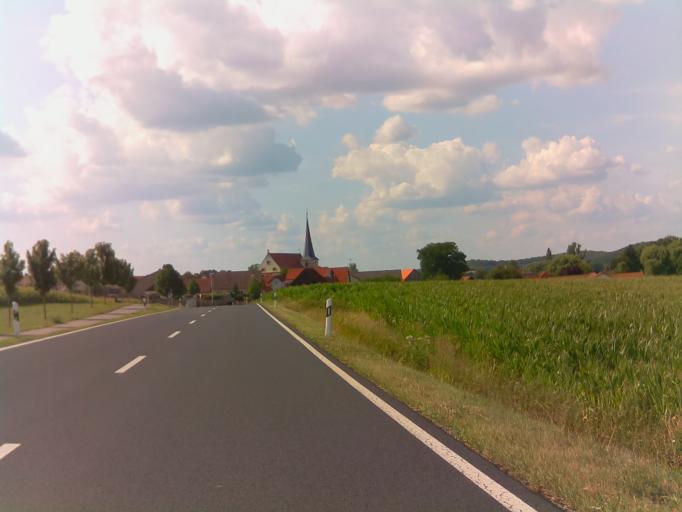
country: DE
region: Bavaria
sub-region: Regierungsbezirk Unterfranken
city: Bundorf
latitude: 50.2687
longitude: 10.5298
